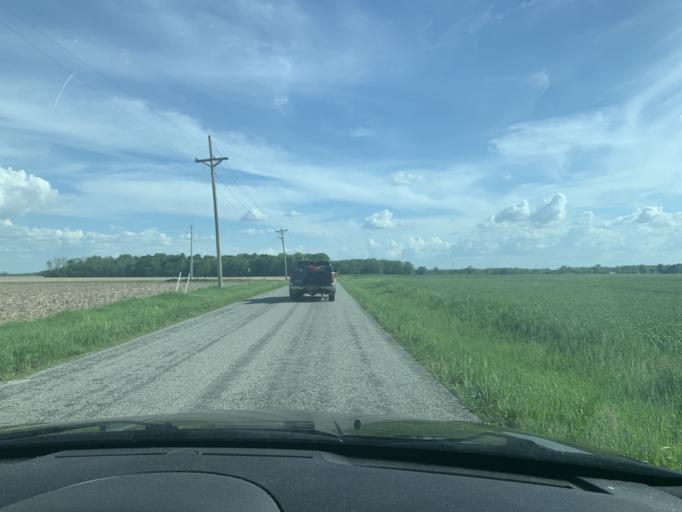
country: US
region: Ohio
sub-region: Logan County
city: De Graff
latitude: 40.2453
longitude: -84.0173
